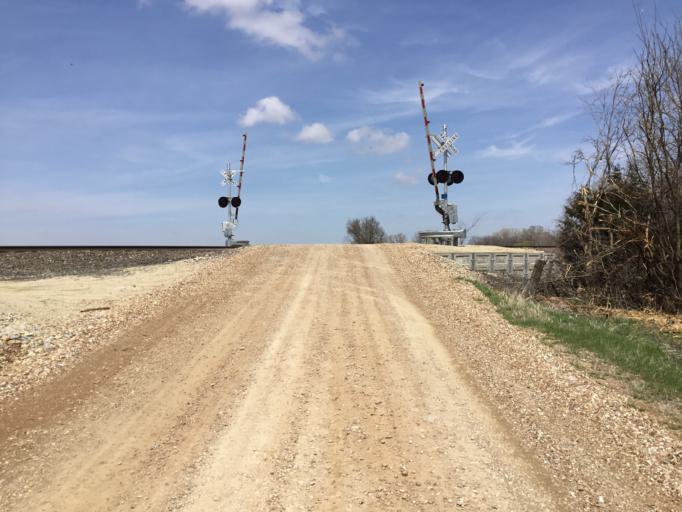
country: US
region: Kansas
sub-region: Butler County
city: Augusta
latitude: 37.6282
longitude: -97.0265
